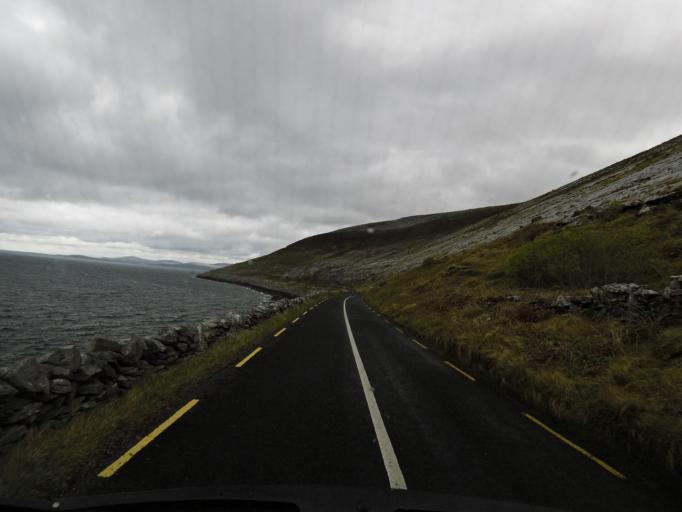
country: IE
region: Connaught
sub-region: County Galway
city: Bearna
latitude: 53.1523
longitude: -9.2582
